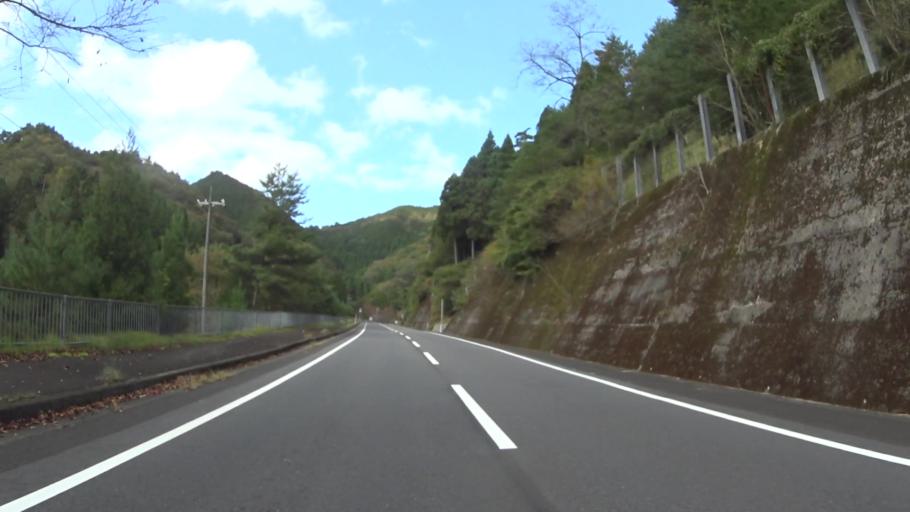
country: JP
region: Hyogo
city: Toyooka
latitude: 35.5211
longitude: 134.9886
